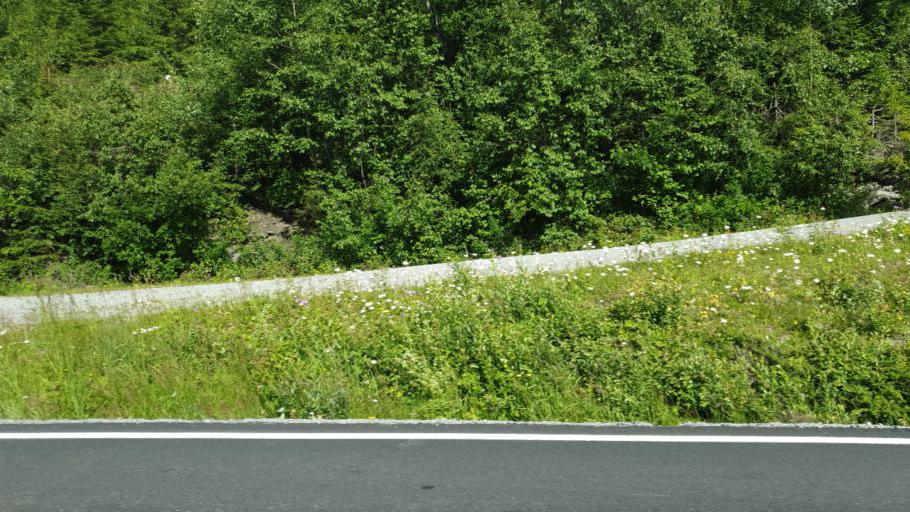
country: NO
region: Oppland
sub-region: Oystre Slidre
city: Heggenes
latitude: 61.1667
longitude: 8.9962
